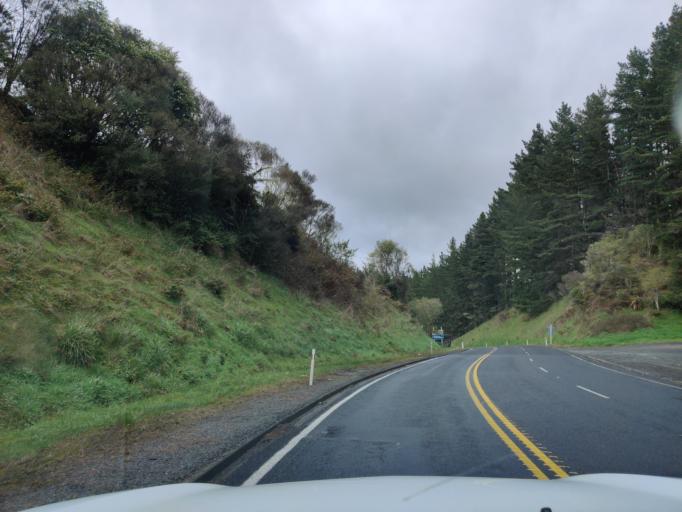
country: NZ
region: Waikato
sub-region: Otorohanga District
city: Otorohanga
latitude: -38.6396
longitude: 175.2065
